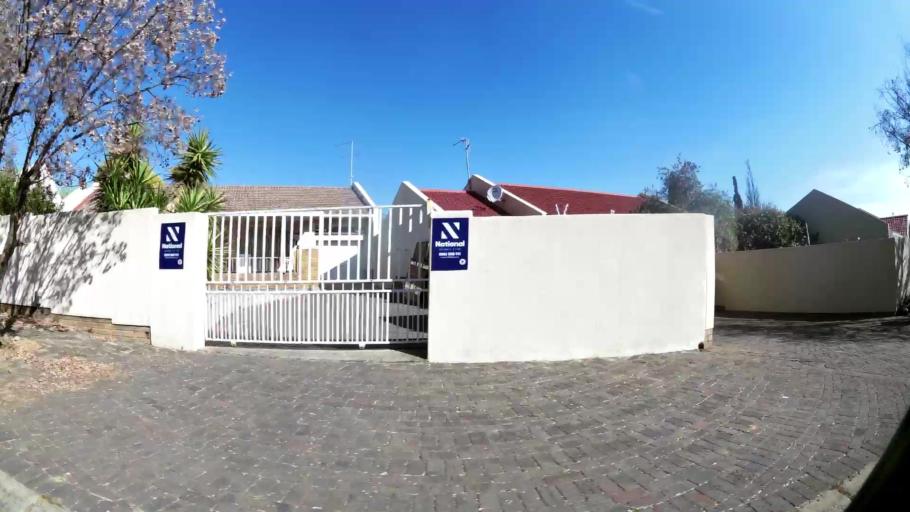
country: ZA
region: Gauteng
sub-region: City of Johannesburg Metropolitan Municipality
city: Roodepoort
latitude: -26.1058
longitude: 27.9678
